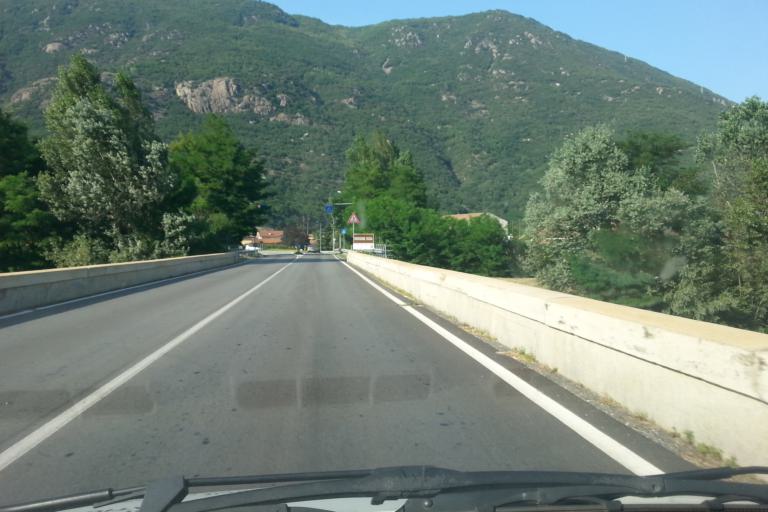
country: IT
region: Piedmont
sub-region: Provincia di Torino
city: Borgone Susa
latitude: 45.1184
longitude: 7.2388
